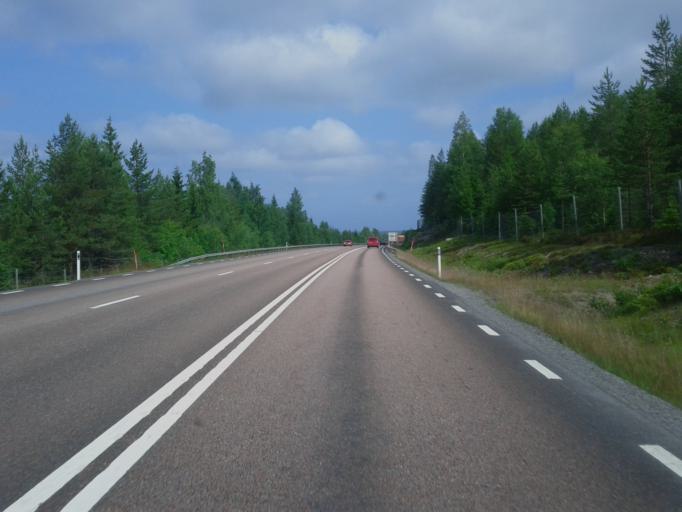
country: SE
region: Vaesterbotten
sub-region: Skelleftea Kommun
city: Burea
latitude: 64.4514
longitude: 21.2844
